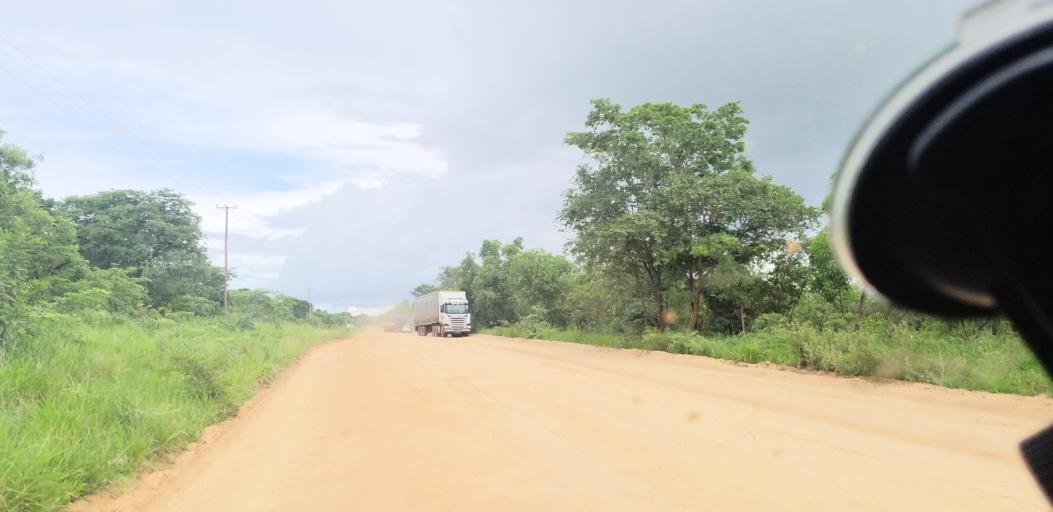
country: ZM
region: Lusaka
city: Chongwe
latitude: -15.1795
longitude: 28.4531
